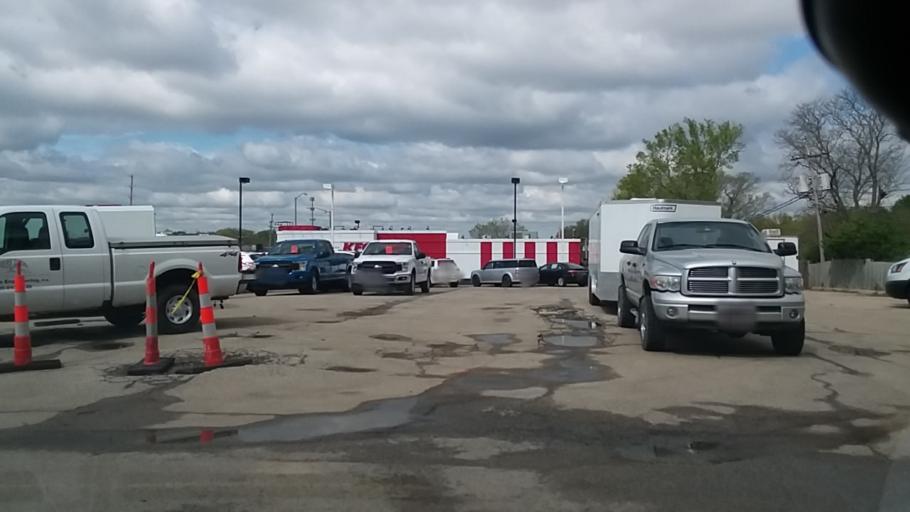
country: US
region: Kansas
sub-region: Douglas County
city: Lawrence
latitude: 38.9432
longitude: -95.2456
